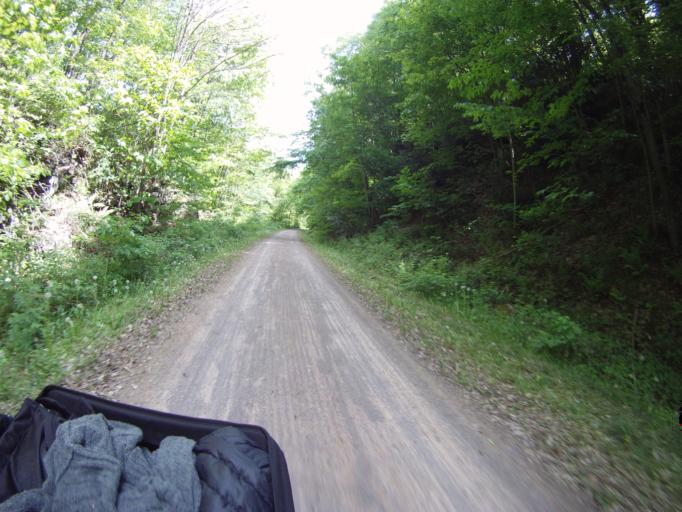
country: US
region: Pennsylvania
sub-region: Somerset County
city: Meyersdale
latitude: 39.8071
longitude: -78.9877
